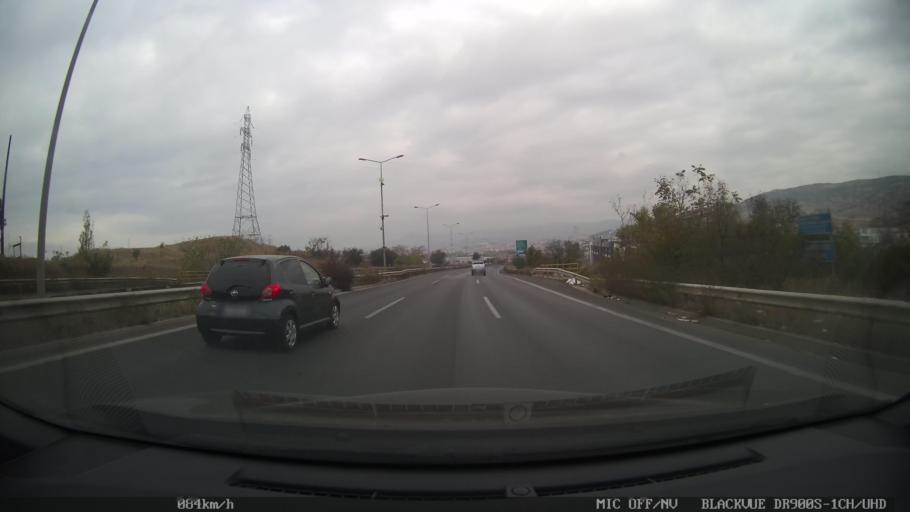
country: GR
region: Central Macedonia
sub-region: Nomos Thessalonikis
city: Polichni
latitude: 40.6647
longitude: 22.9631
